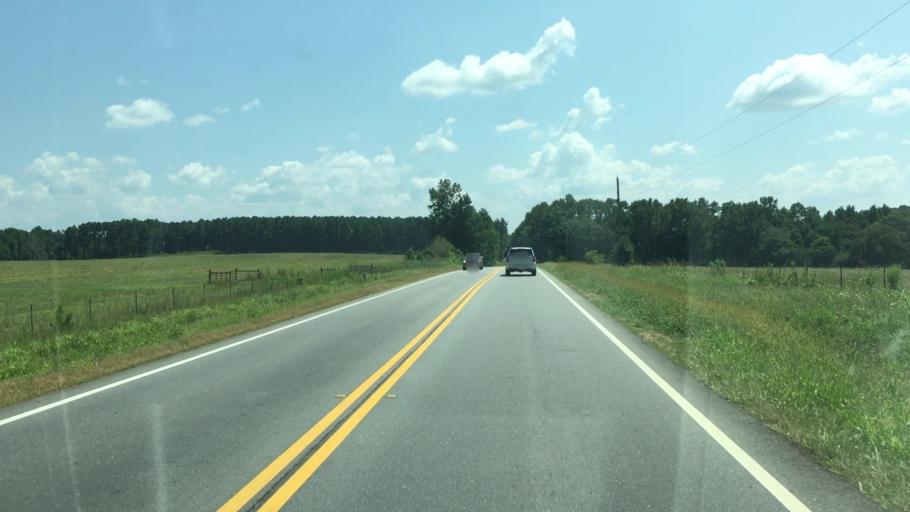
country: US
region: Georgia
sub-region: Oconee County
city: Watkinsville
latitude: 33.7960
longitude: -83.4253
